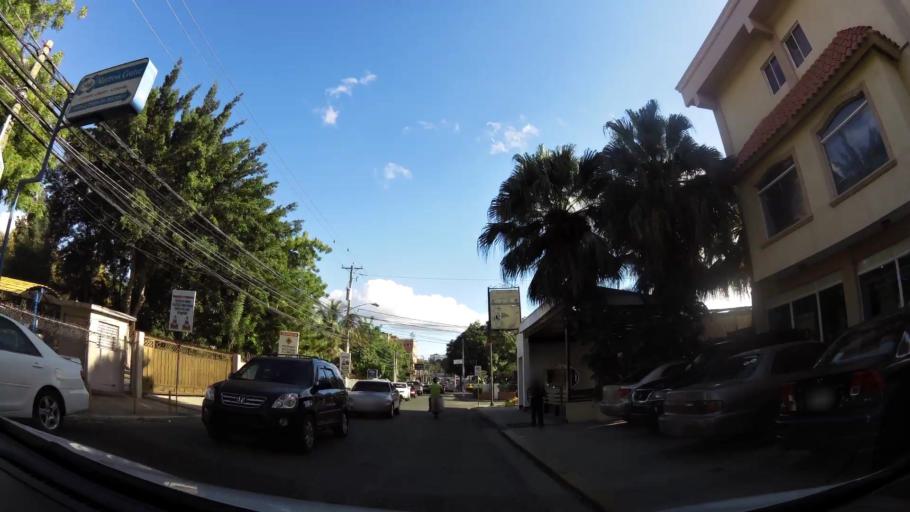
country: DO
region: Santiago
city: Santiago de los Caballeros
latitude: 19.4638
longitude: -70.6890
